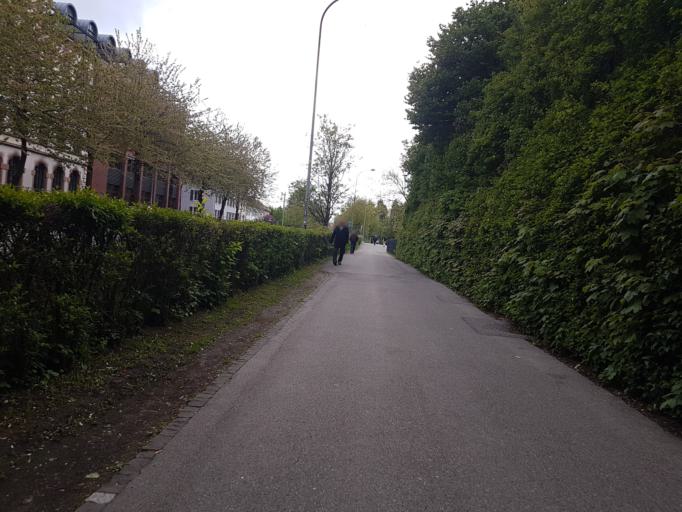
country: CH
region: Bern
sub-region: Biel/Bienne District
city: Biel/Bienne
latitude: 47.1353
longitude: 7.2418
